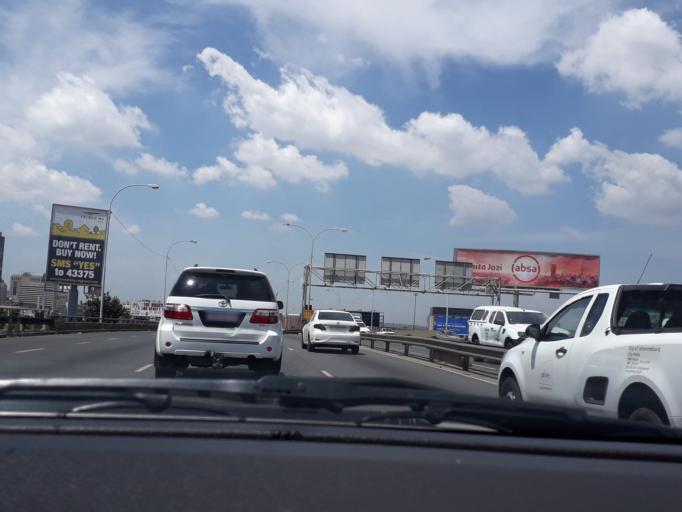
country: ZA
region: Gauteng
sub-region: City of Johannesburg Metropolitan Municipality
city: Johannesburg
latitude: -26.1954
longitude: 28.0284
